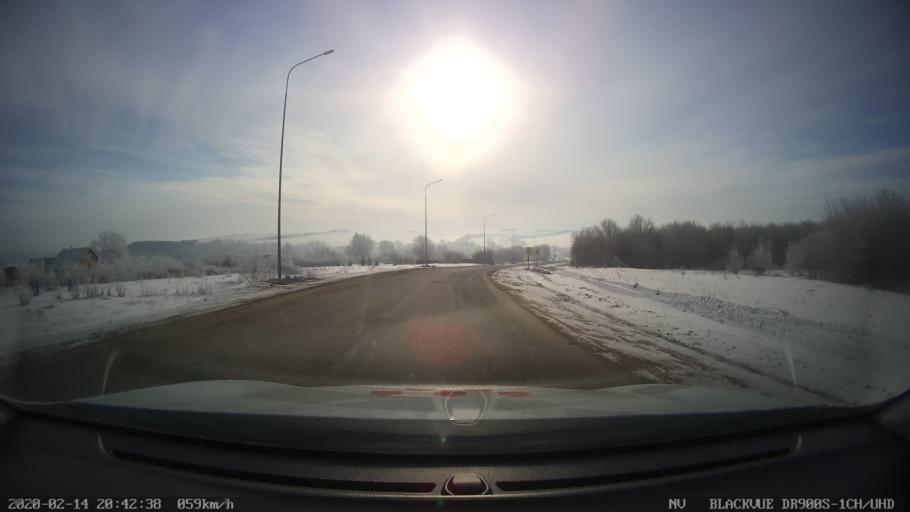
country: RU
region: Tatarstan
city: Kuybyshevskiy Zaton
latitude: 55.3156
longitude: 49.1441
